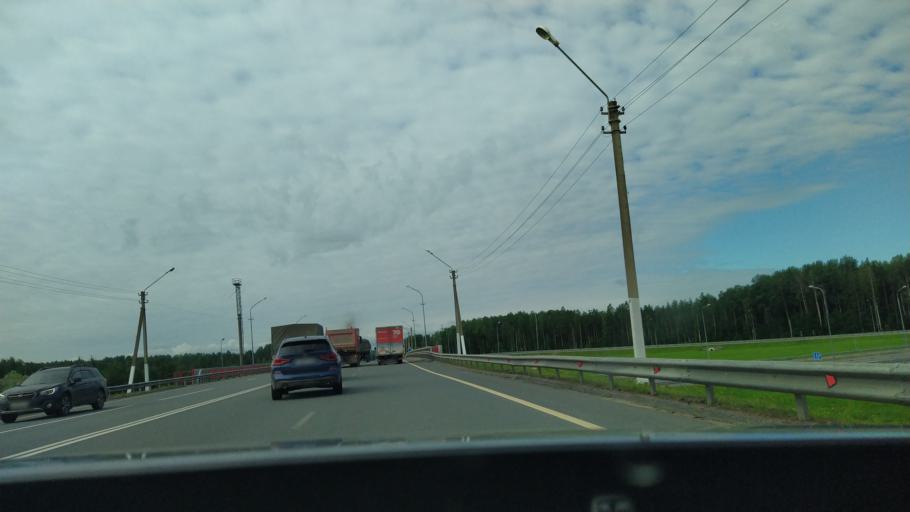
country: RU
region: Leningrad
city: Ul'yanovka
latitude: 59.6063
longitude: 30.7603
